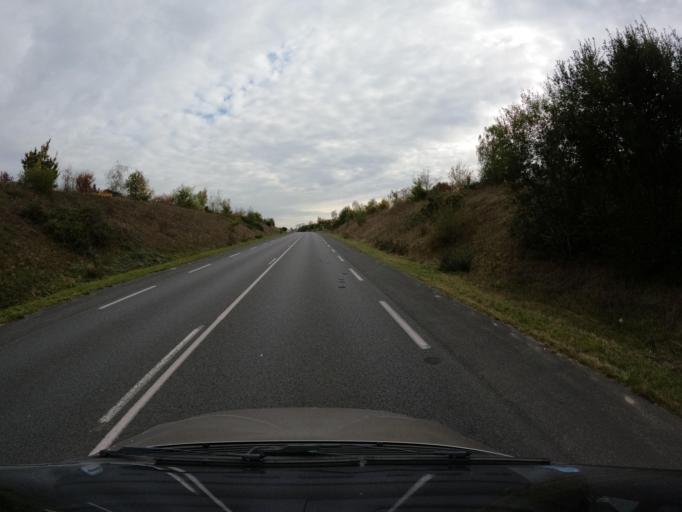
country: FR
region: Pays de la Loire
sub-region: Departement de la Loire-Atlantique
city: Getigne
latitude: 47.0889
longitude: -1.2630
